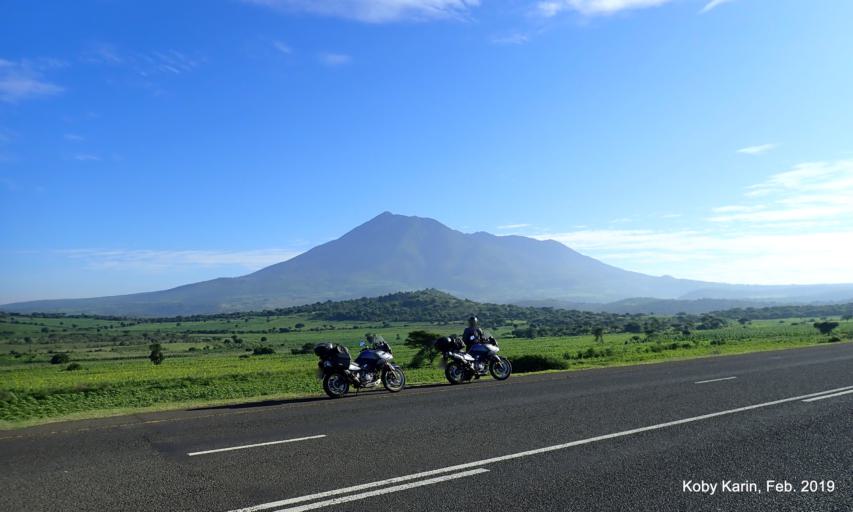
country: TZ
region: Manyara
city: Katesh
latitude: -4.5185
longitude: 35.3426
